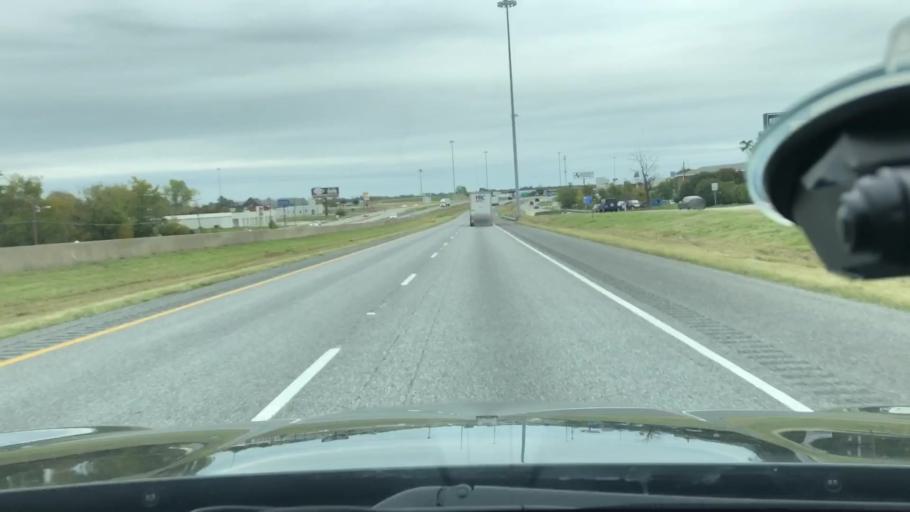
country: US
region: Texas
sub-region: Hunt County
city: Greenville
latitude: 33.1098
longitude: -96.1020
